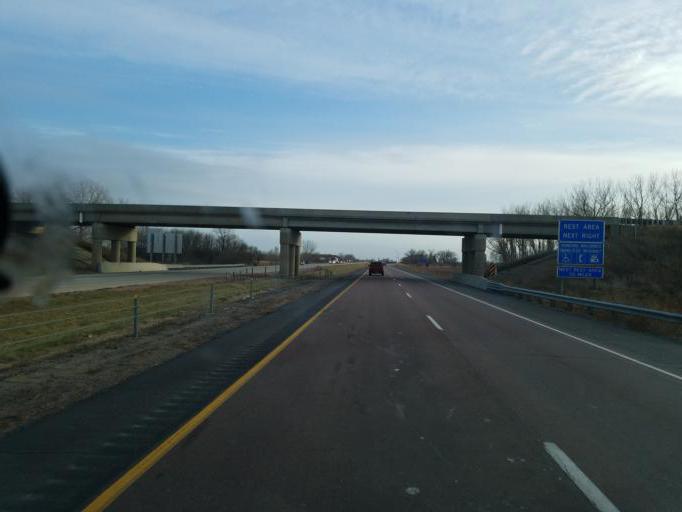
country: US
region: Iowa
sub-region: Woodbury County
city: Sergeant Bluff
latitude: 42.3822
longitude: -96.3587
